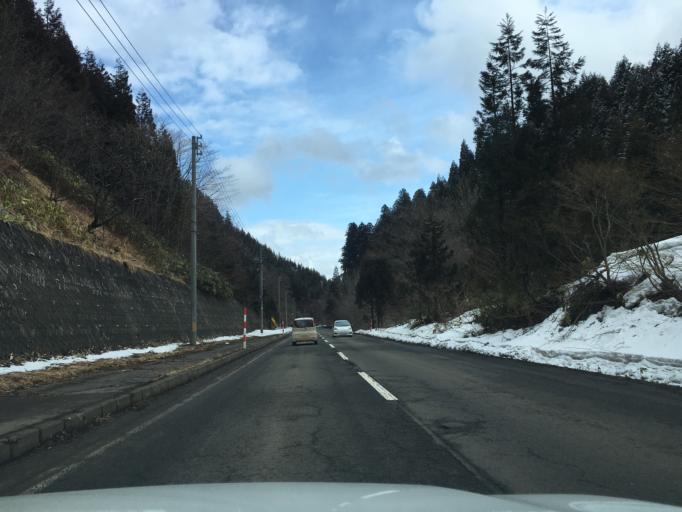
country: JP
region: Akita
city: Takanosu
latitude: 39.9940
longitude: 140.2508
